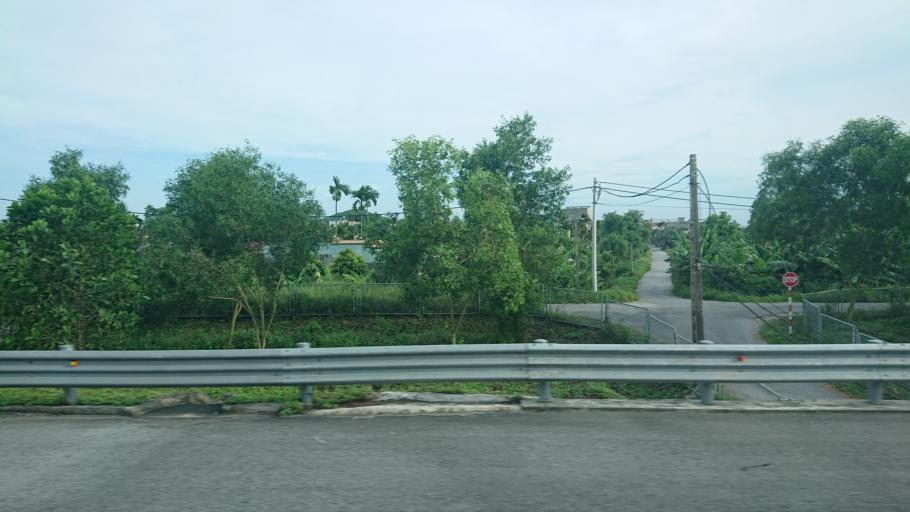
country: VN
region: Hai Phong
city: Nui Doi
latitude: 20.7655
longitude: 106.6635
